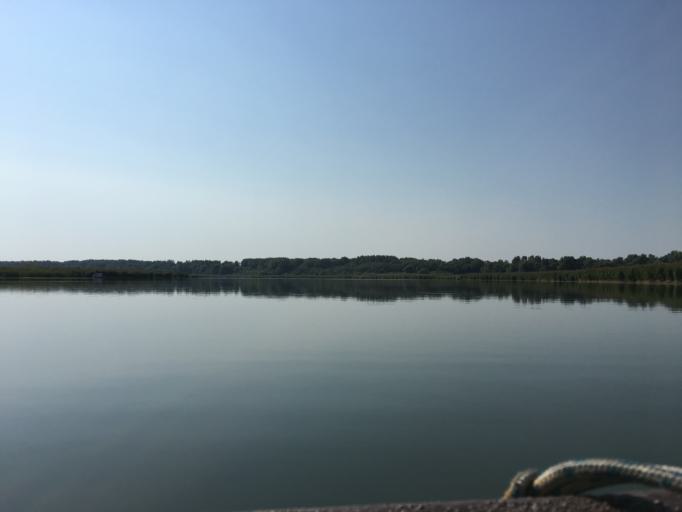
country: HU
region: Jasz-Nagykun-Szolnok
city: Tiszafured
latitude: 47.6548
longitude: 20.7318
